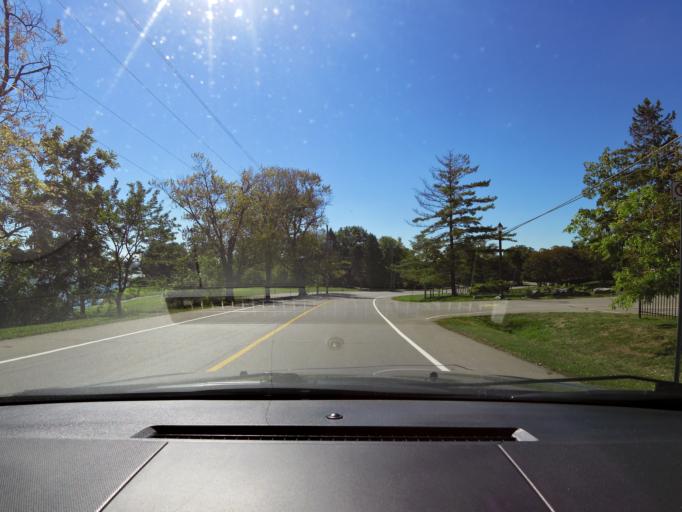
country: CA
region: Ontario
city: Hamilton
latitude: 43.3090
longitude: -79.8286
